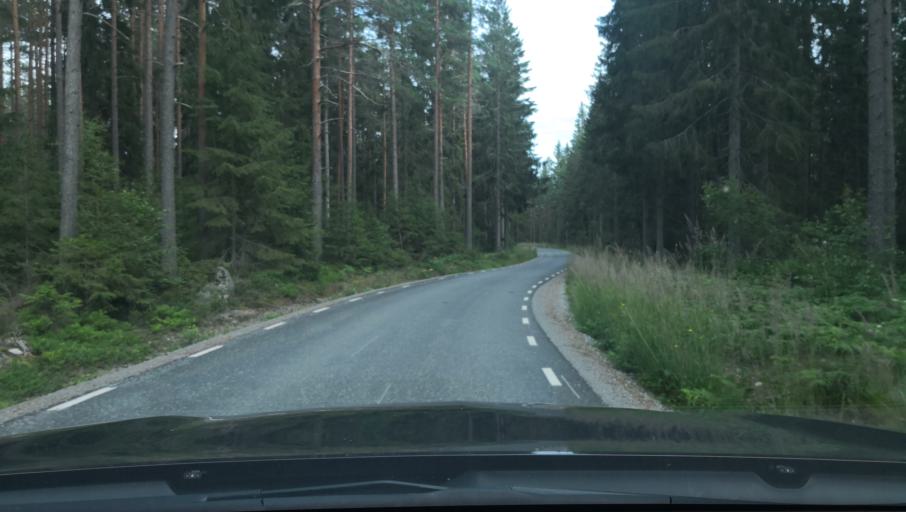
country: SE
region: Vaestmanland
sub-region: Surahammars Kommun
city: Surahammar
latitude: 59.6743
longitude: 16.1194
